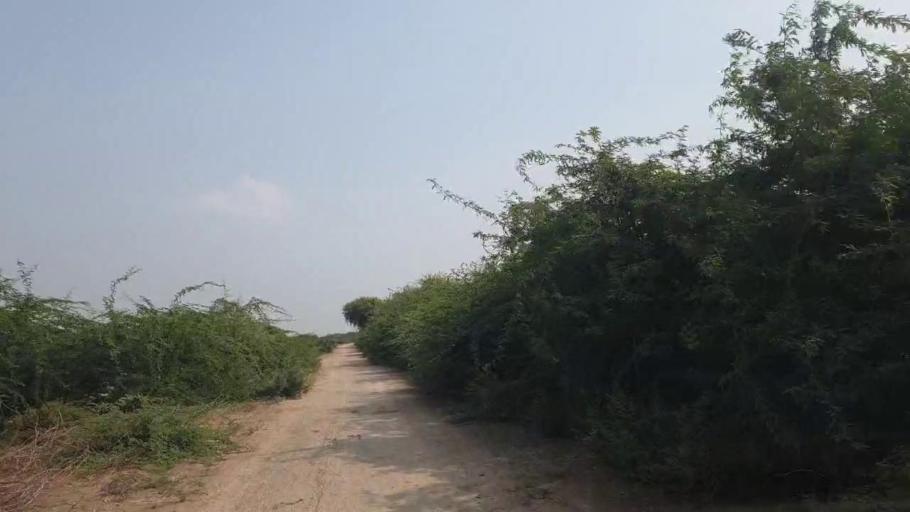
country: PK
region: Sindh
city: Badin
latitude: 24.5475
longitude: 68.6931
